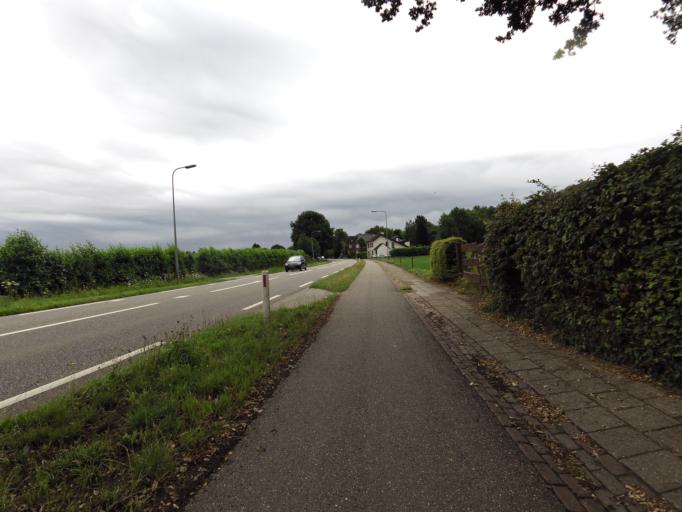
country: NL
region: Limburg
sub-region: Gemeente Voerendaal
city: Klimmen
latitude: 50.8957
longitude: 5.8520
